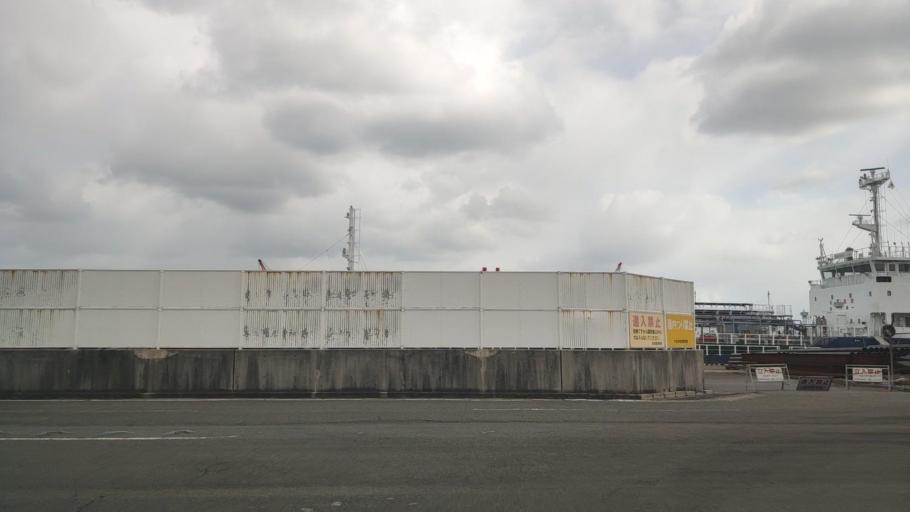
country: JP
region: Ehime
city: Saijo
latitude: 34.0619
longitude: 133.0186
